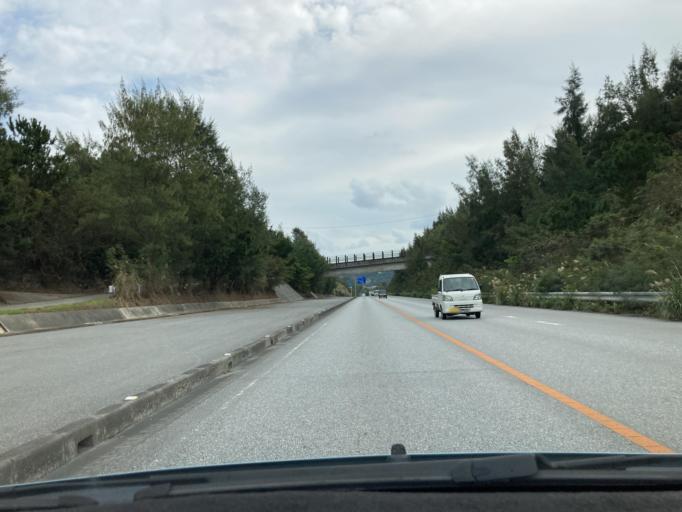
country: JP
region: Okinawa
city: Ishikawa
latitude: 26.5046
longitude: 127.8745
